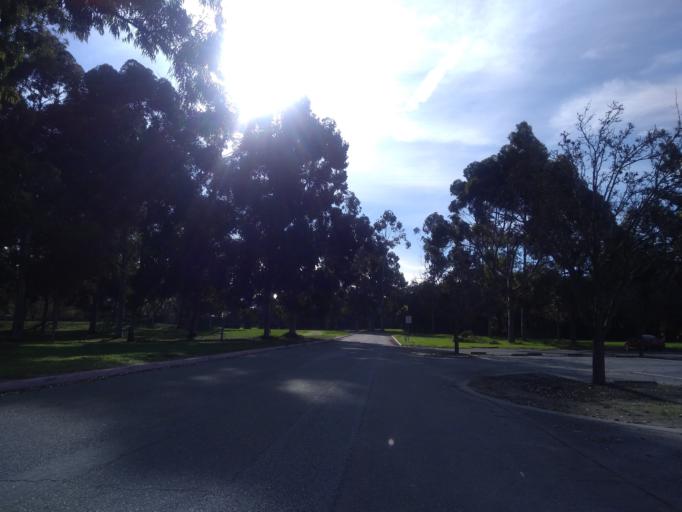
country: US
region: California
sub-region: Santa Clara County
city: Sunnyvale
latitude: 37.4118
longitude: -121.9987
